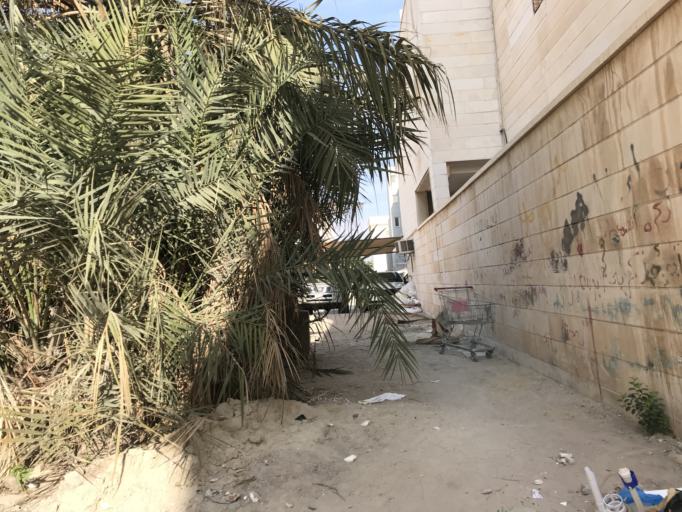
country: KW
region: Muhafazat Hawalli
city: Ar Rumaythiyah
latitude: 29.3041
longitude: 48.0743
